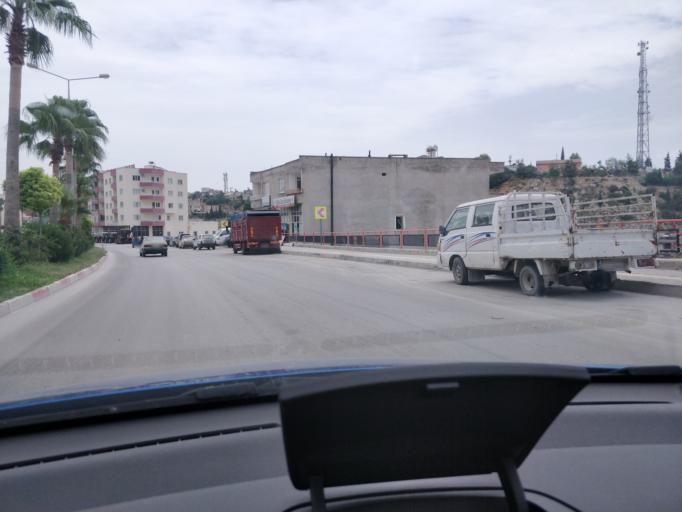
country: TR
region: Mersin
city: Mut
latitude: 36.6463
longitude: 33.4291
